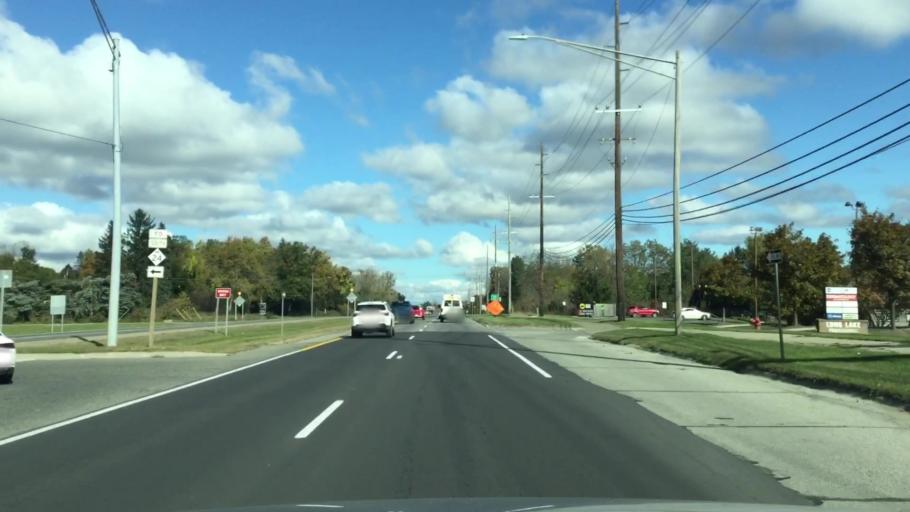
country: US
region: Michigan
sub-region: Oakland County
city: Lake Orion
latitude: 42.7919
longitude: -83.2460
